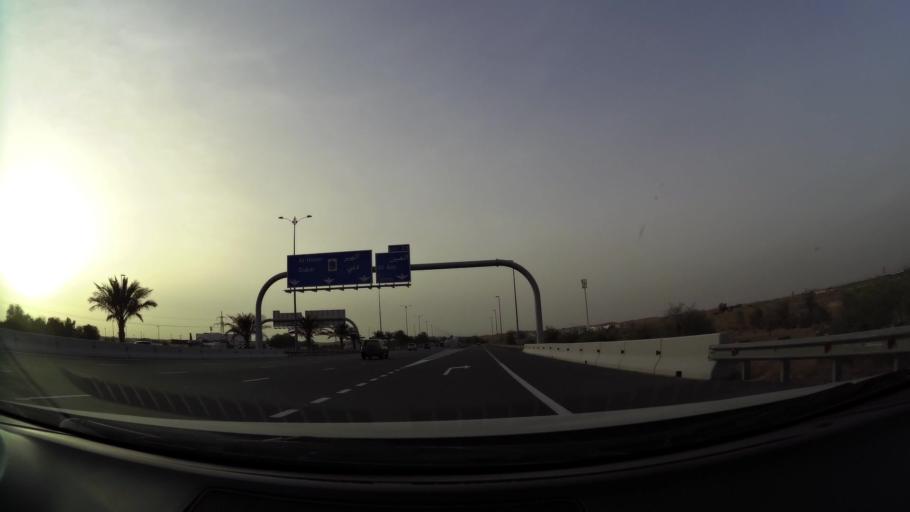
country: OM
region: Al Buraimi
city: Al Buraymi
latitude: 24.3965
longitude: 55.7969
